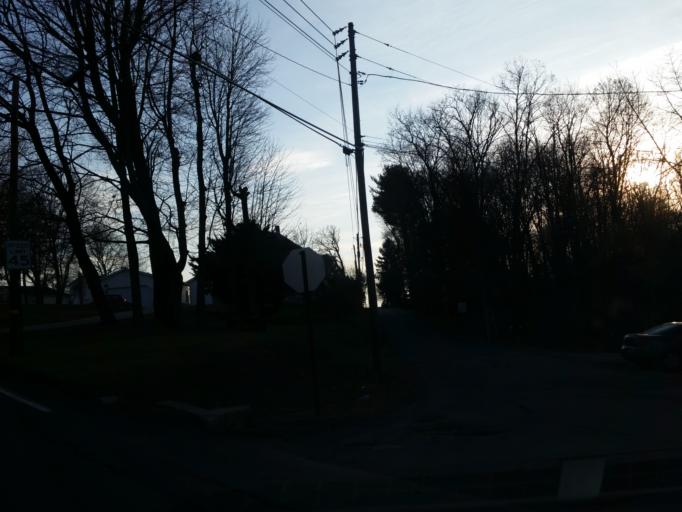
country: US
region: Pennsylvania
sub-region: Schuylkill County
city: Minersville
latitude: 40.6842
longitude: -76.2675
